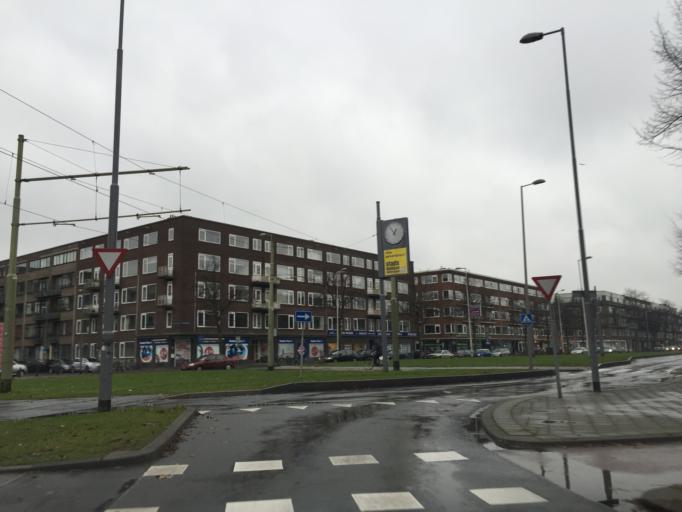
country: NL
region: South Holland
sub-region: Gemeente Rotterdam
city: Rotterdam
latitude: 51.9316
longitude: 4.4622
